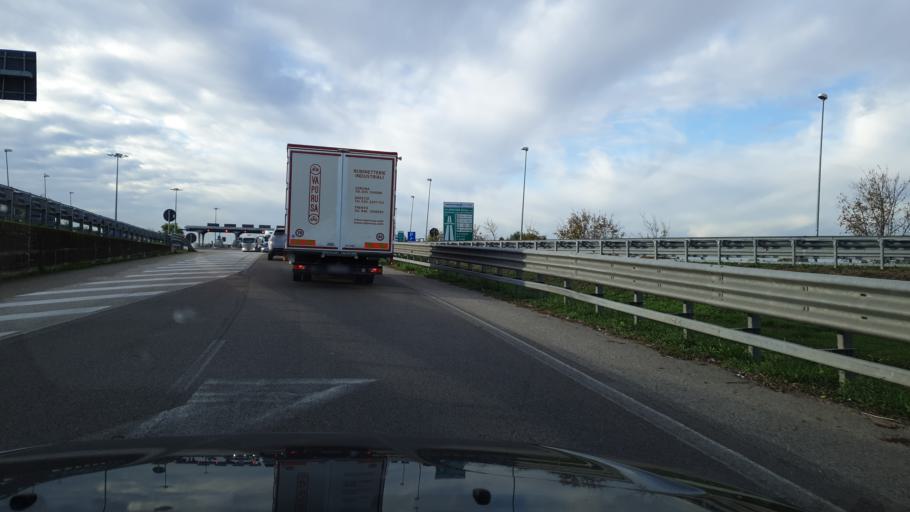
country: IT
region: Veneto
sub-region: Provincia di Rovigo
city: Villamarzana
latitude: 45.0210
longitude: 11.7014
